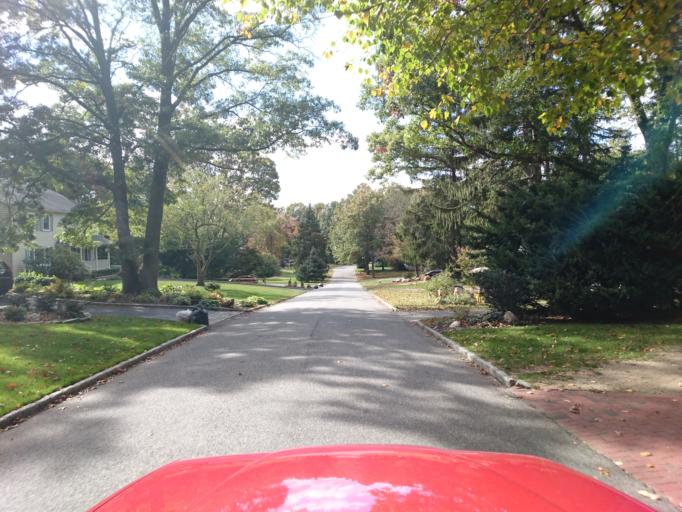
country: US
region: New York
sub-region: Nassau County
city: Locust Valley
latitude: 40.8773
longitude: -73.6062
